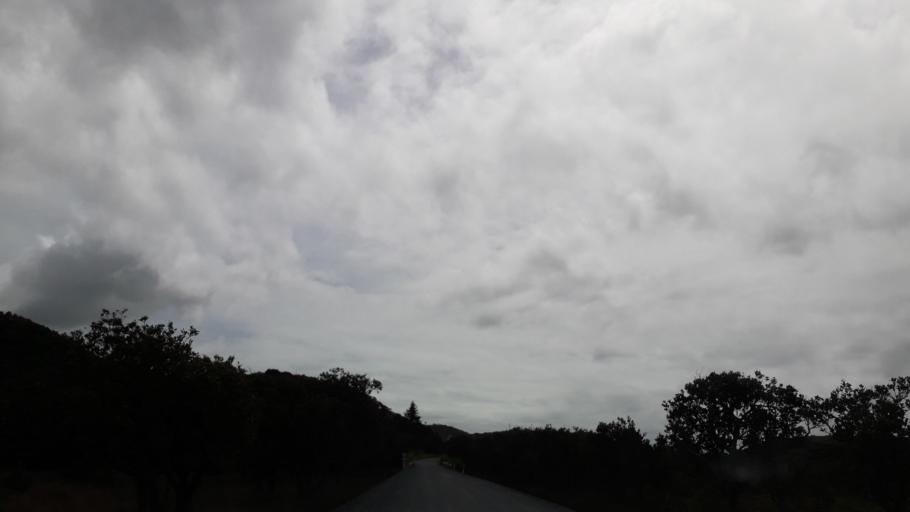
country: NZ
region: Northland
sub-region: Far North District
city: Taipa
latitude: -35.0290
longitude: 173.5594
